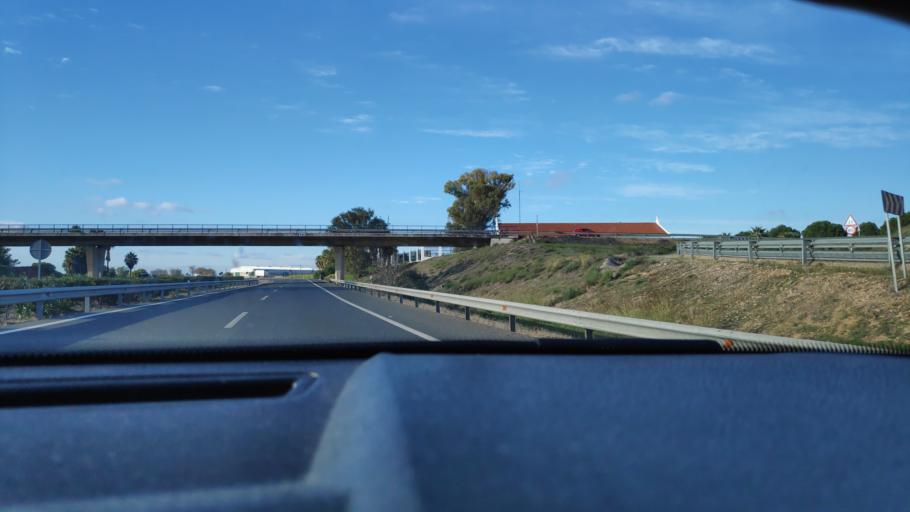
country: ES
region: Andalusia
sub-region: Provincia de Sevilla
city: La Luisiana
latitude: 37.5241
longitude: -5.2586
